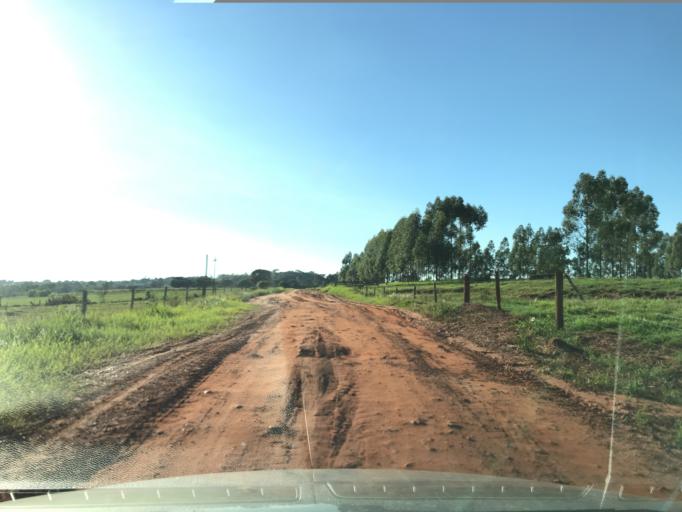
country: BR
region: Parana
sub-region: Ipora
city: Ipora
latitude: -23.9951
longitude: -53.7264
